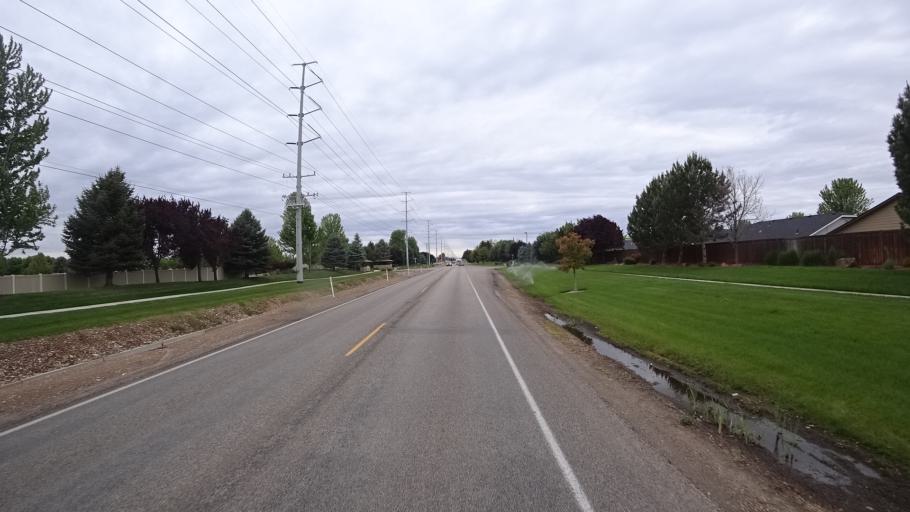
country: US
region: Idaho
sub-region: Ada County
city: Meridian
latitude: 43.6483
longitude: -116.4002
